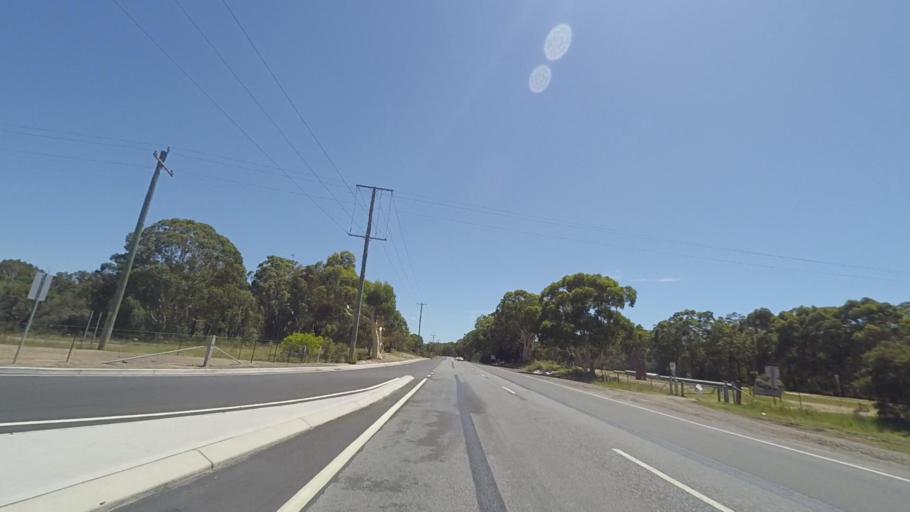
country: AU
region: New South Wales
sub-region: Port Stephens Shire
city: Medowie
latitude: -32.7841
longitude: 151.8575
